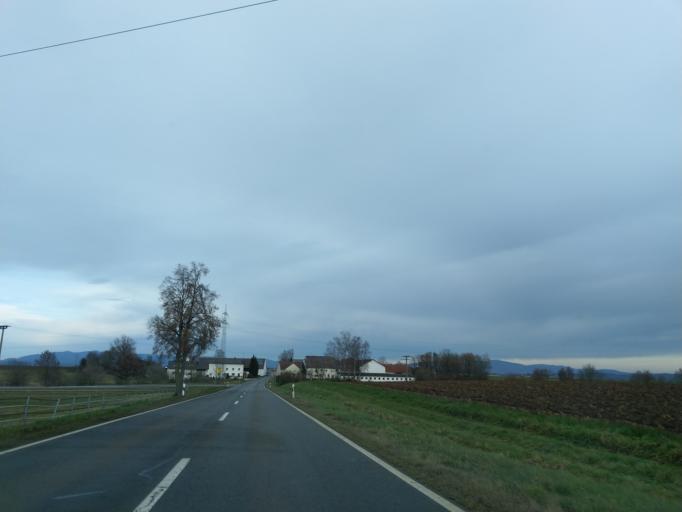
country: DE
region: Bavaria
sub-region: Lower Bavaria
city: Osterhofen
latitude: 48.6725
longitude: 12.9930
